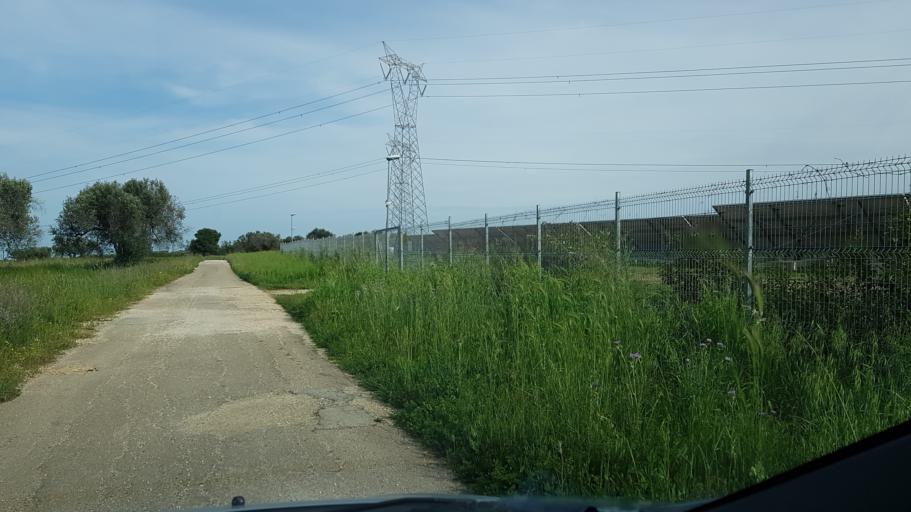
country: IT
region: Apulia
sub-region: Provincia di Brindisi
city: Tuturano
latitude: 40.5539
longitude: 17.9289
